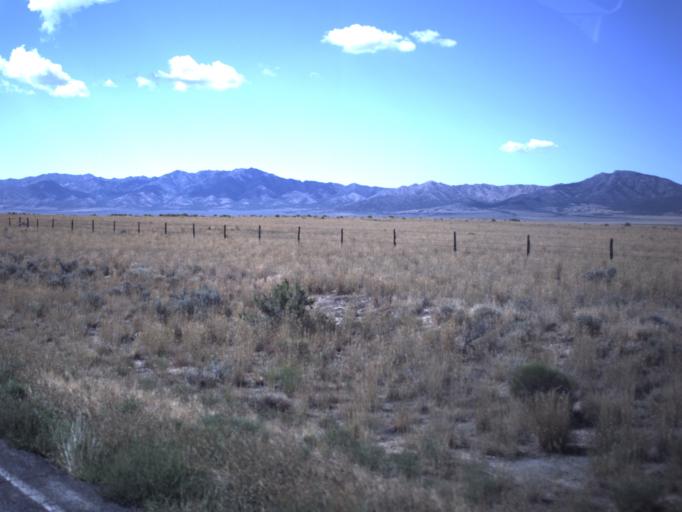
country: US
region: Utah
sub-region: Tooele County
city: Tooele
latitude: 40.1327
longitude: -112.4308
